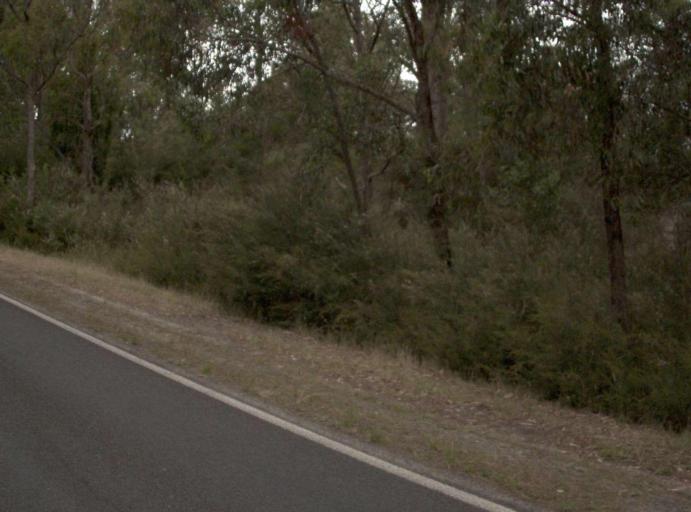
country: AU
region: Victoria
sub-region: Latrobe
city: Traralgon
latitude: -38.5389
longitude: 146.8447
